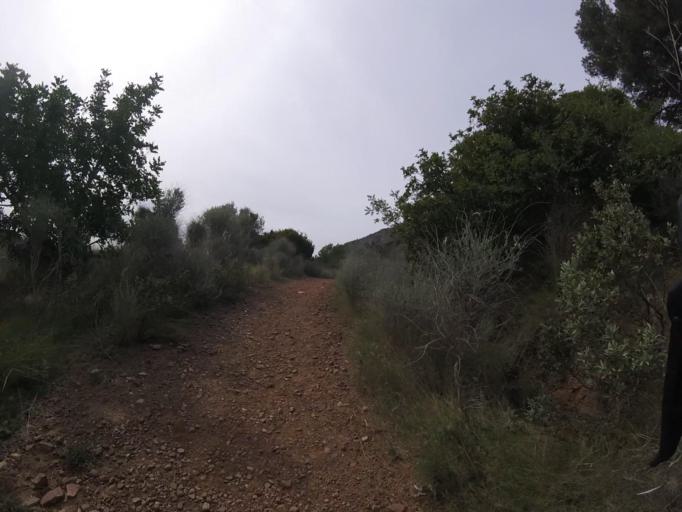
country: ES
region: Valencia
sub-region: Provincia de Castello
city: Benicassim
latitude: 40.0717
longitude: 0.0350
